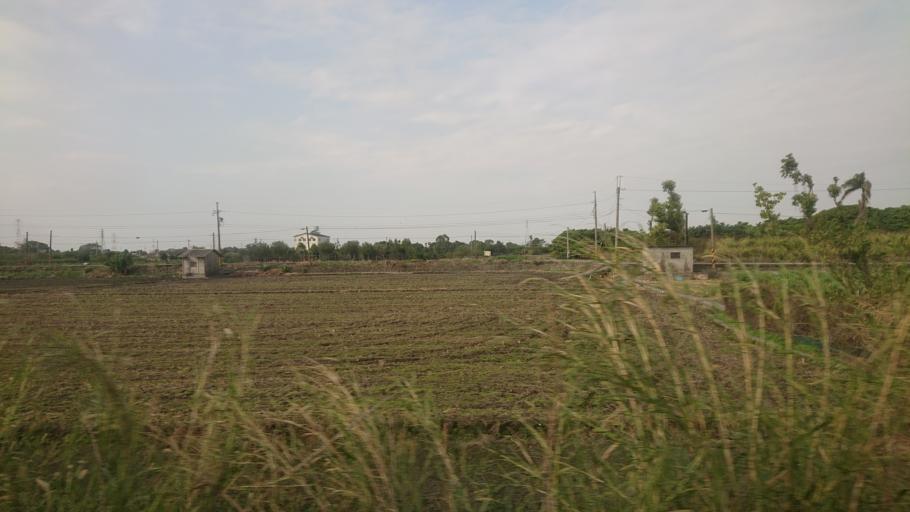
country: TW
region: Taiwan
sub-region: Nantou
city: Nantou
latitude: 23.8917
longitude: 120.5816
